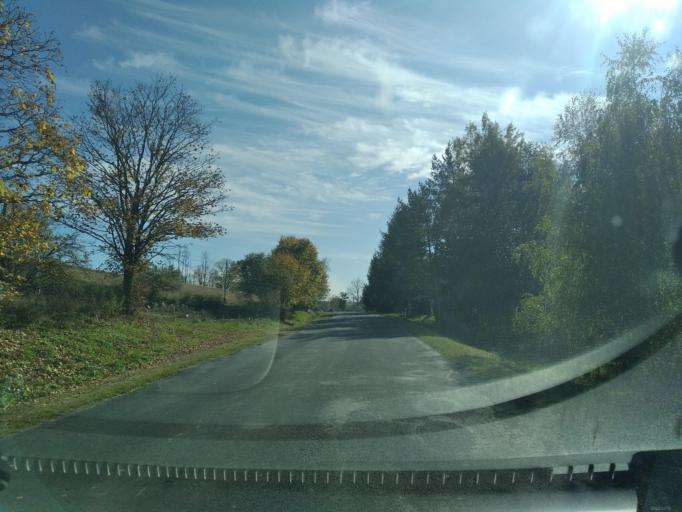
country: PL
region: Subcarpathian Voivodeship
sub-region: Powiat sanocki
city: Komancza
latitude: 49.3942
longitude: 21.9830
